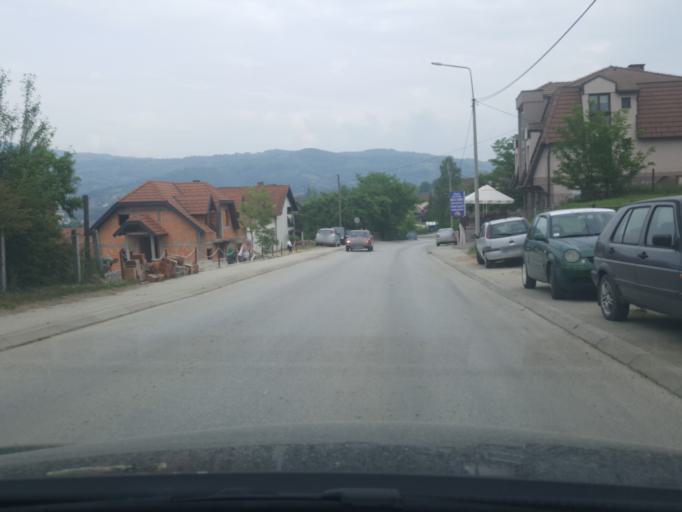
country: RS
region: Central Serbia
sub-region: Zlatiborski Okrug
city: Bajina Basta
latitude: 43.9670
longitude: 19.5511
